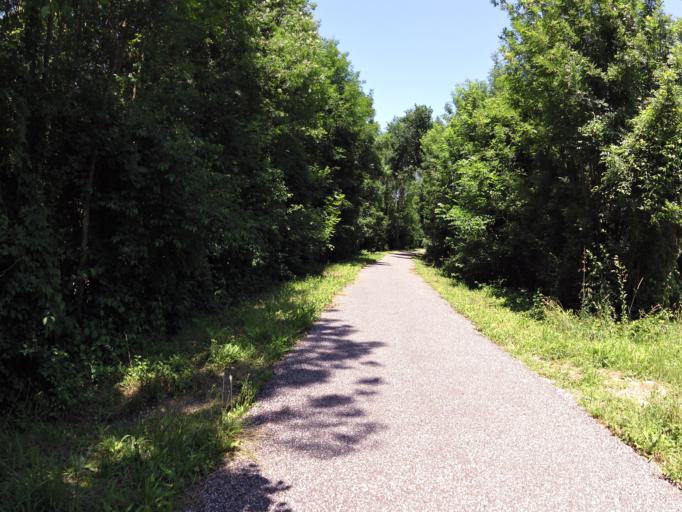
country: FR
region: Aquitaine
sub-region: Departement des Pyrenees-Atlantiques
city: Salies-de-Bearn
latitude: 43.4477
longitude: -0.9945
